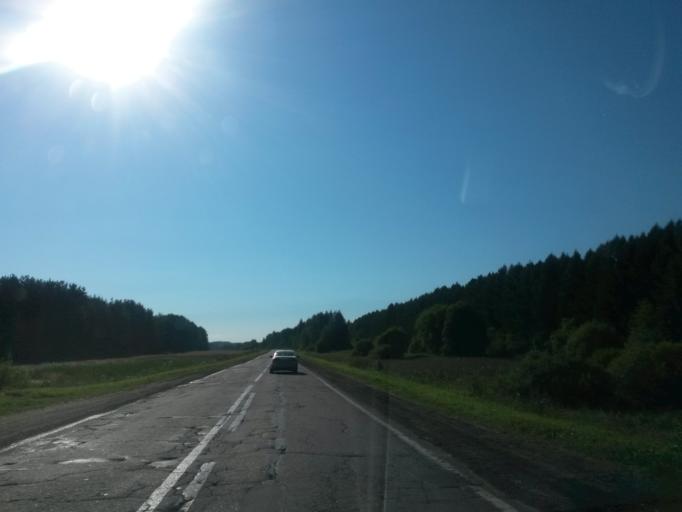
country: RU
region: Jaroslavl
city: Krasnyye Tkachi
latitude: 57.3927
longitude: 39.6808
